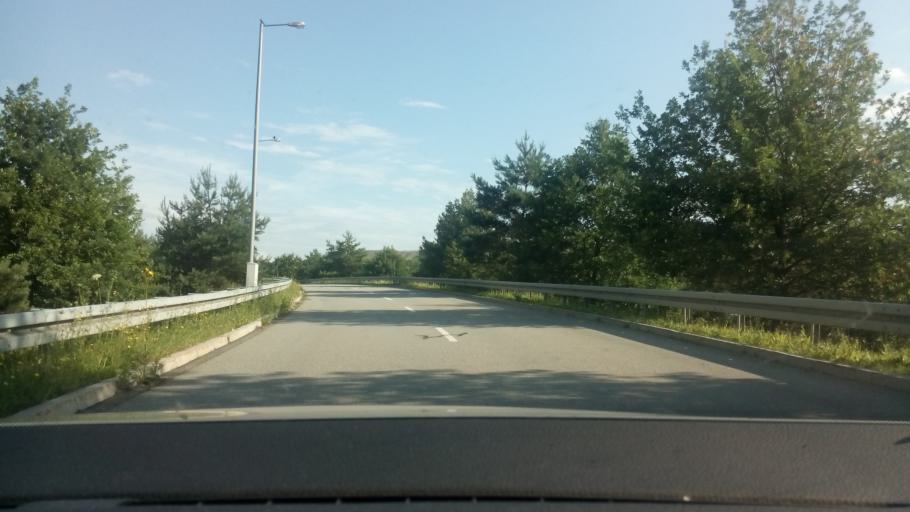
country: DE
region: Bavaria
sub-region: Upper Bavaria
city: Unterfoehring
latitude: 48.2201
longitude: 11.6273
